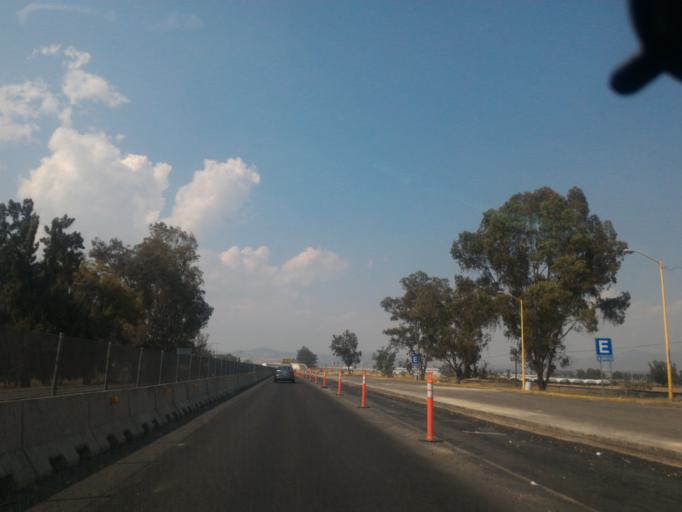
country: MX
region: Jalisco
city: Ciudad Guzman
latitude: 19.7124
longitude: -103.5026
